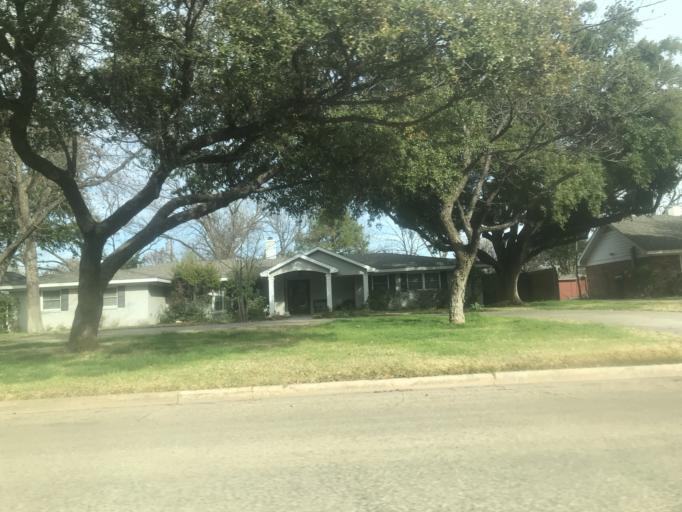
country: US
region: Texas
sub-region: Taylor County
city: Abilene
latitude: 32.4293
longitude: -99.7704
